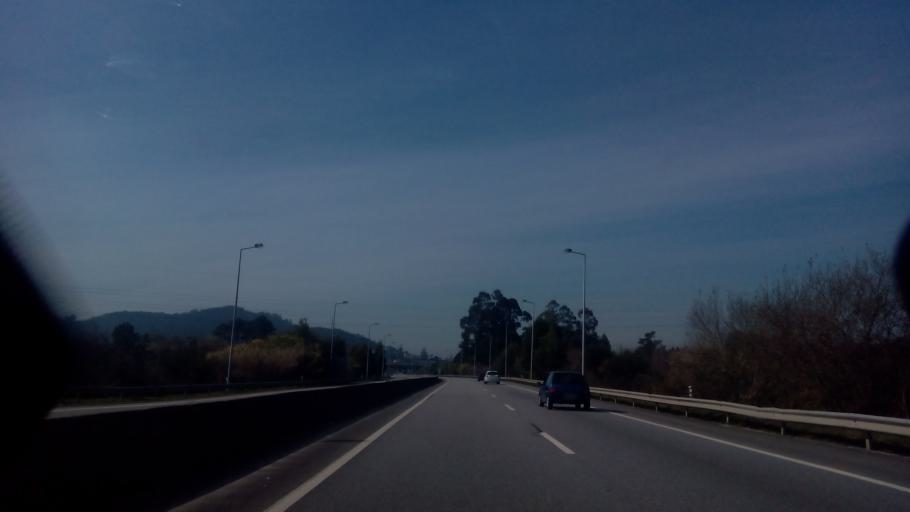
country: PT
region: Viana do Castelo
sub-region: Viana do Castelo
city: Darque
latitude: 41.6842
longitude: -8.7683
